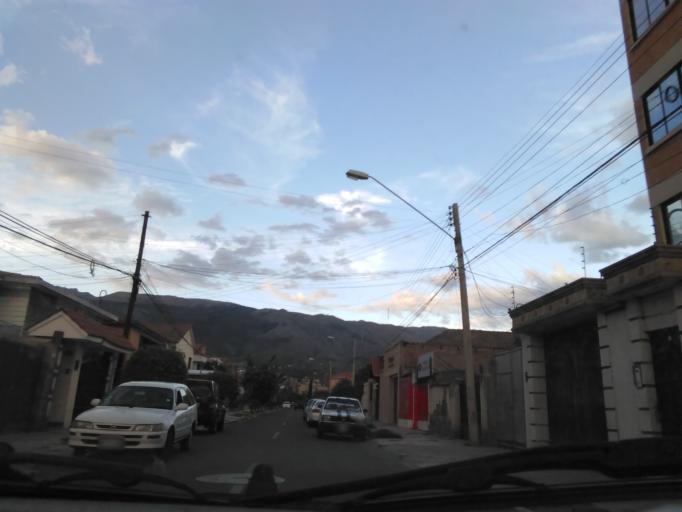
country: BO
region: Cochabamba
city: Cochabamba
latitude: -17.3854
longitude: -66.1669
